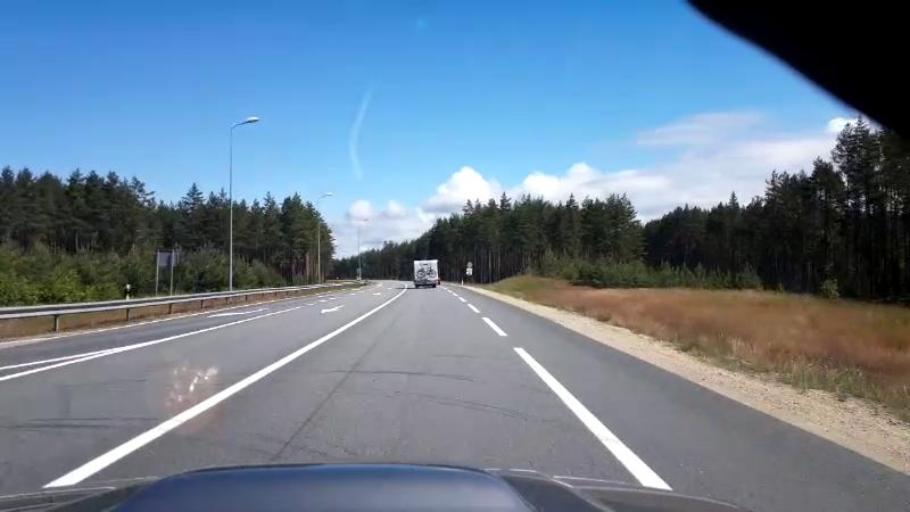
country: LV
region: Saulkrastu
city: Saulkrasti
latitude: 57.2315
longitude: 24.4248
